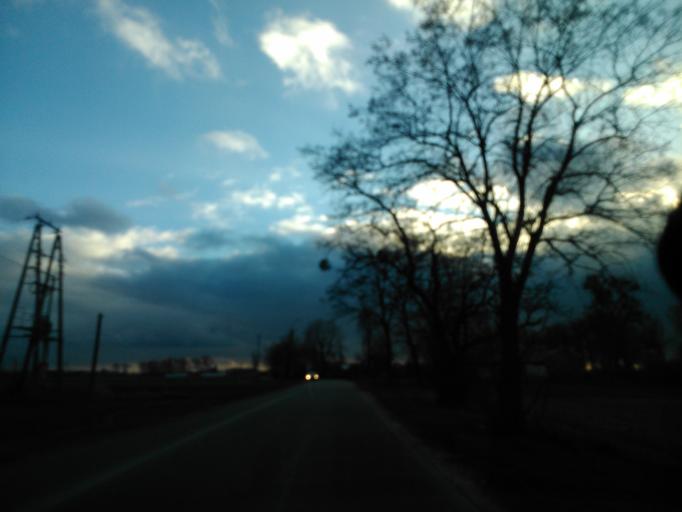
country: PL
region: Masovian Voivodeship
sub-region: Powiat warszawski zachodni
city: Blonie
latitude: 52.2183
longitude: 20.6526
